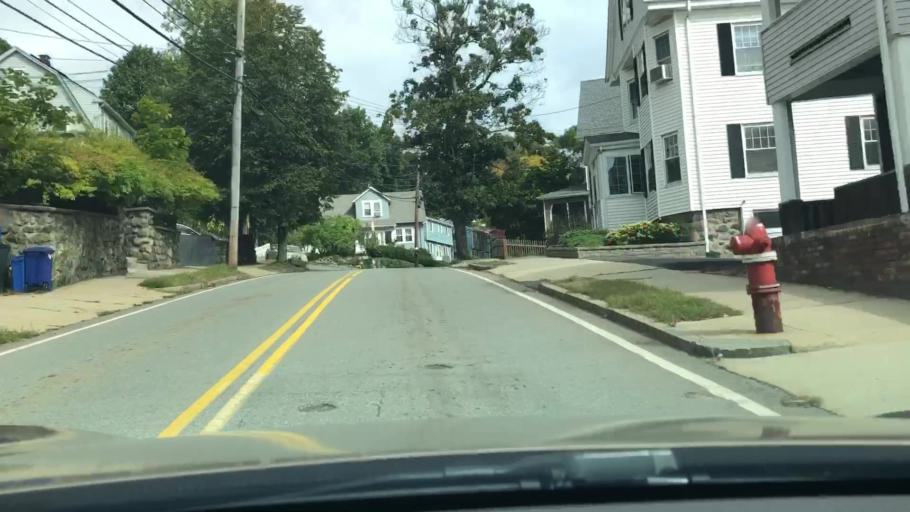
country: US
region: Massachusetts
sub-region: Middlesex County
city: Arlington
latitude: 42.4264
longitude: -71.1816
